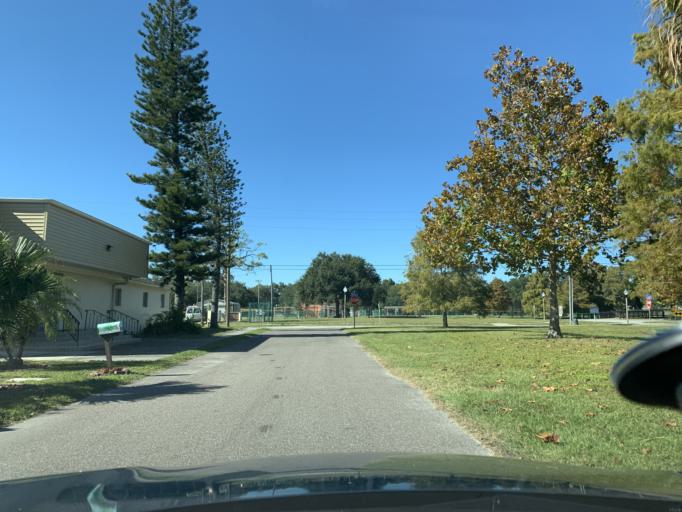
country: US
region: Florida
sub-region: Pinellas County
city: Gulfport
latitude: 27.7517
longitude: -82.7059
